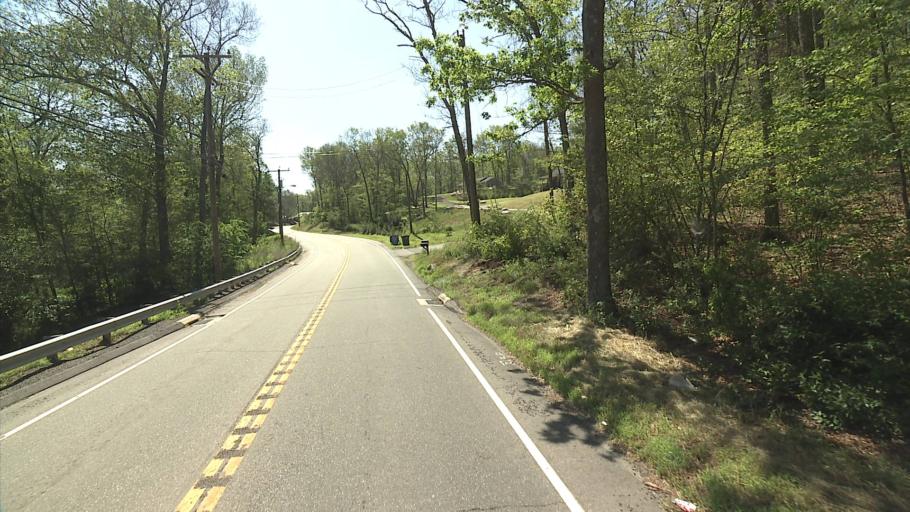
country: US
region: Connecticut
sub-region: Windham County
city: Moosup
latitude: 41.7180
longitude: -71.8489
